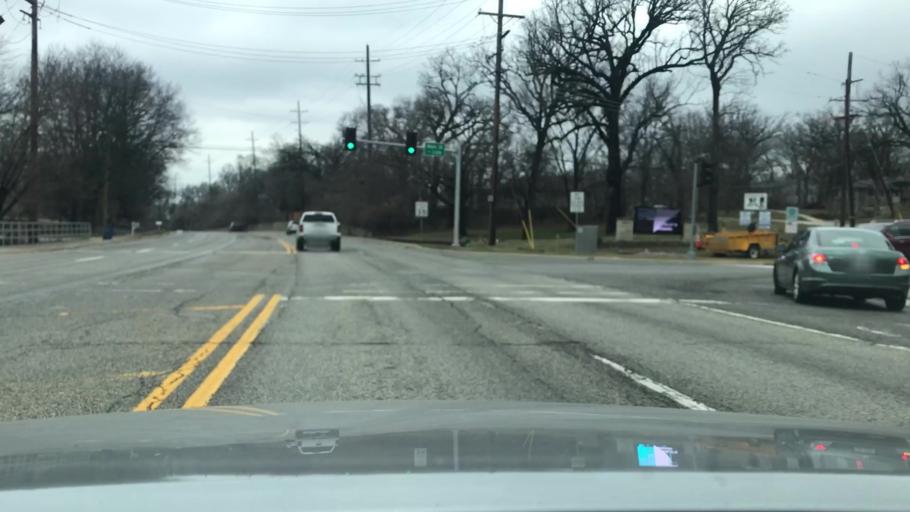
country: US
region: Illinois
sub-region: DuPage County
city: Lisle
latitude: 41.7897
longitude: -88.0744
